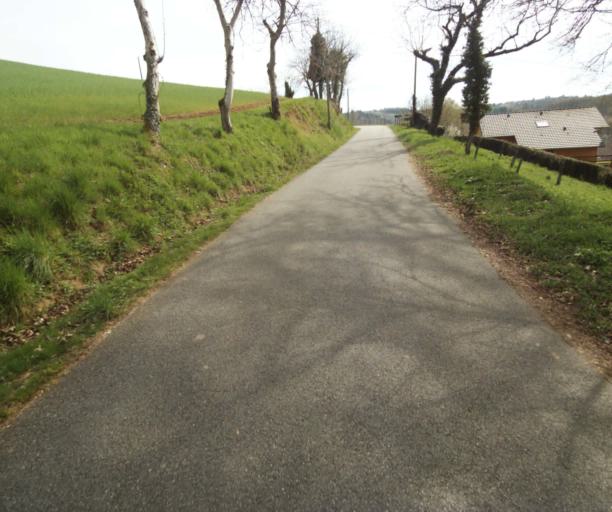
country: FR
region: Limousin
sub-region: Departement de la Correze
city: Naves
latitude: 45.3228
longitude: 1.8052
